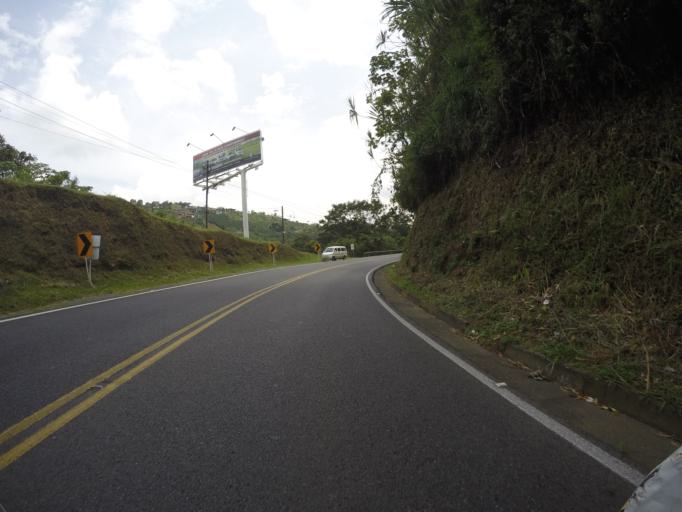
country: CO
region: Risaralda
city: Pereira
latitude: 4.7880
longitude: -75.6958
